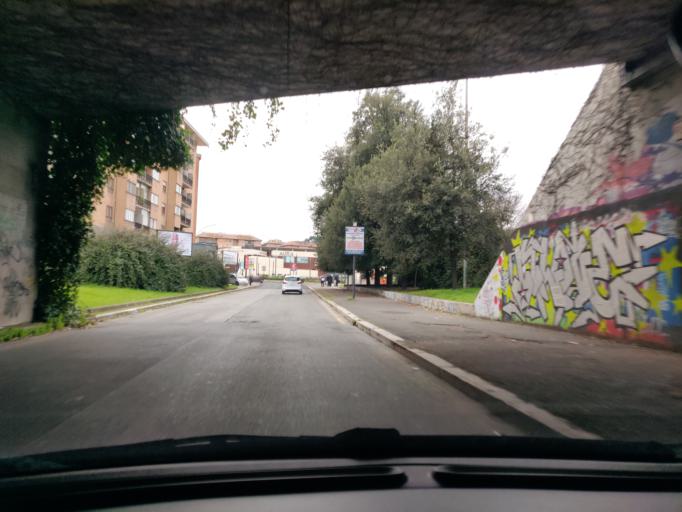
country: VA
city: Vatican City
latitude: 41.9026
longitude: 12.4419
